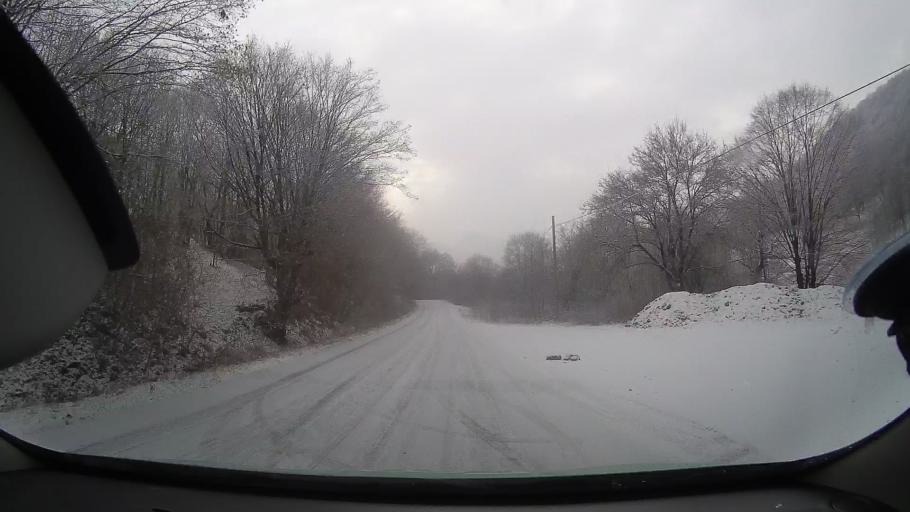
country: RO
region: Alba
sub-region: Comuna Rimetea
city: Rimetea
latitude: 46.4913
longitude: 23.5795
